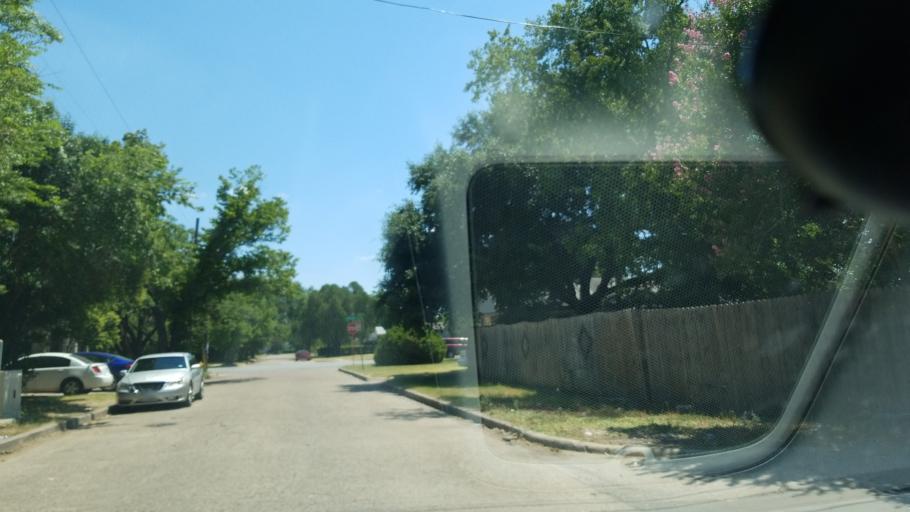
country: US
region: Texas
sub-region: Dallas County
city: Cockrell Hill
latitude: 32.7209
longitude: -96.8512
